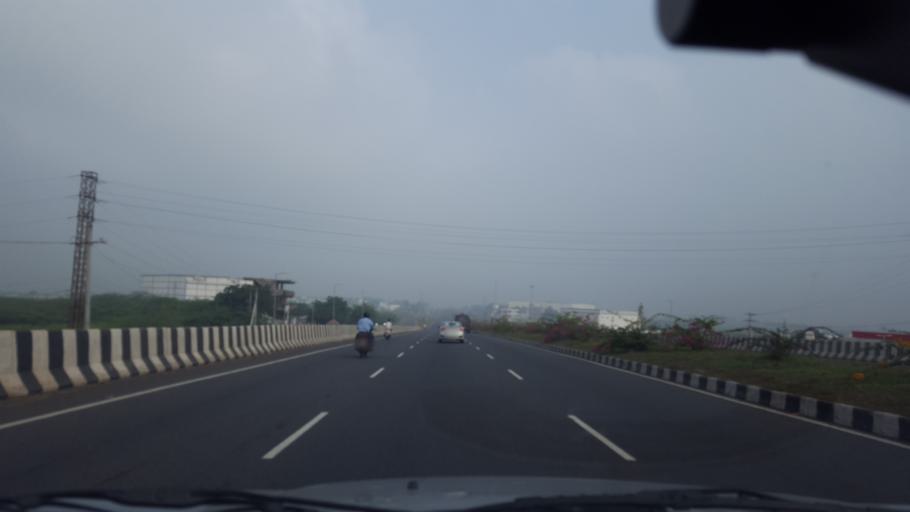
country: IN
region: Andhra Pradesh
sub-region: Prakasam
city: Ongole
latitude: 15.5538
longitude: 80.0551
